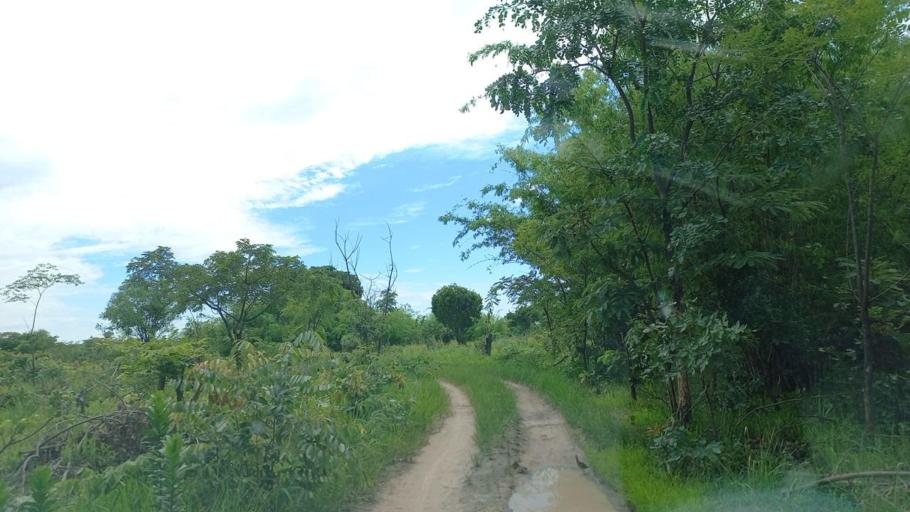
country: ZM
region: Copperbelt
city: Kitwe
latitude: -12.7895
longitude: 28.3938
